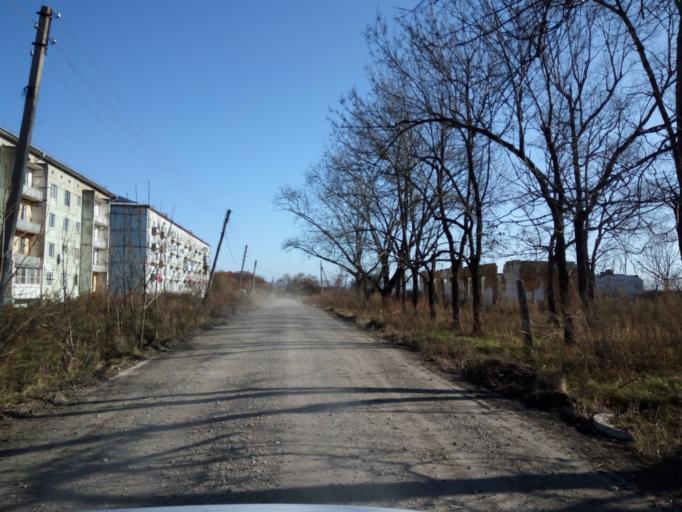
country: RU
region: Primorskiy
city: Dal'nerechensk
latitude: 45.9414
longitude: 133.6801
